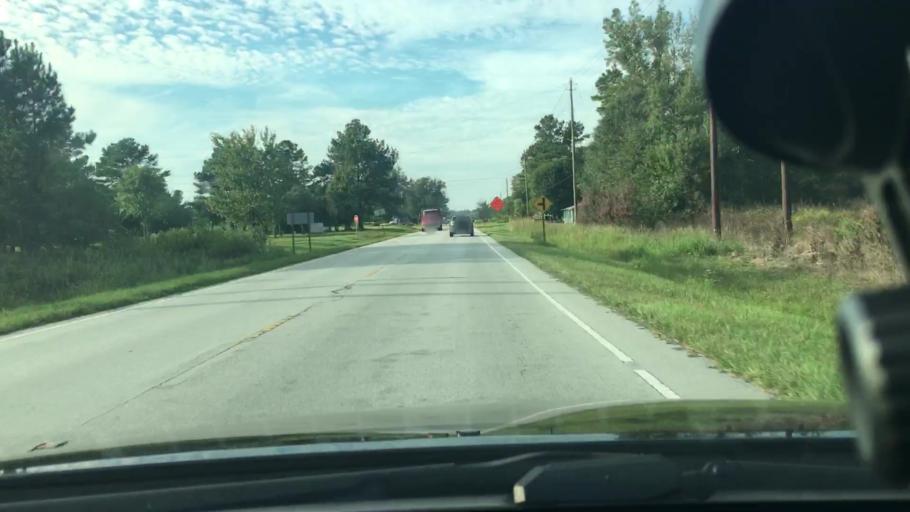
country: US
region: North Carolina
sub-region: Pitt County
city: Windsor
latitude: 35.4919
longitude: -77.3071
